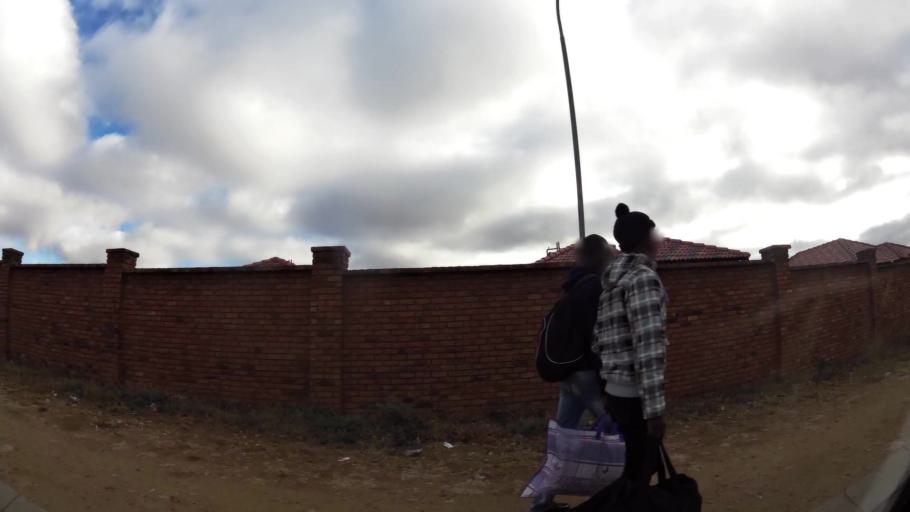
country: ZA
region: Limpopo
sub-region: Capricorn District Municipality
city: Polokwane
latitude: -23.9212
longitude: 29.4445
